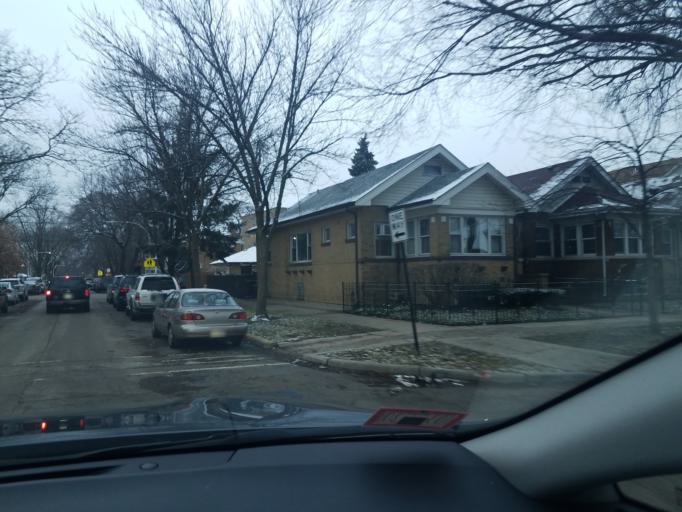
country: US
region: Illinois
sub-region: Cook County
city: Lincolnwood
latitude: 41.9577
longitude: -87.6996
